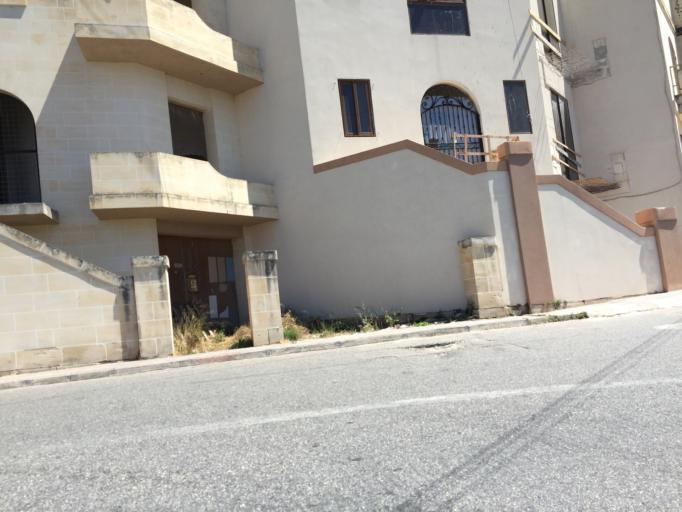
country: MT
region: Is-Swieqi
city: Swieqi
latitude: 35.9145
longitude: 14.4788
